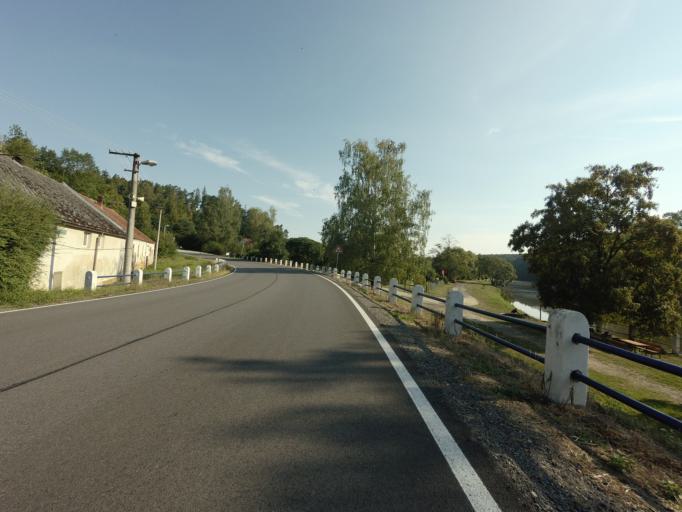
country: CZ
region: Jihocesky
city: Tyn nad Vltavou
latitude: 49.2536
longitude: 14.4199
